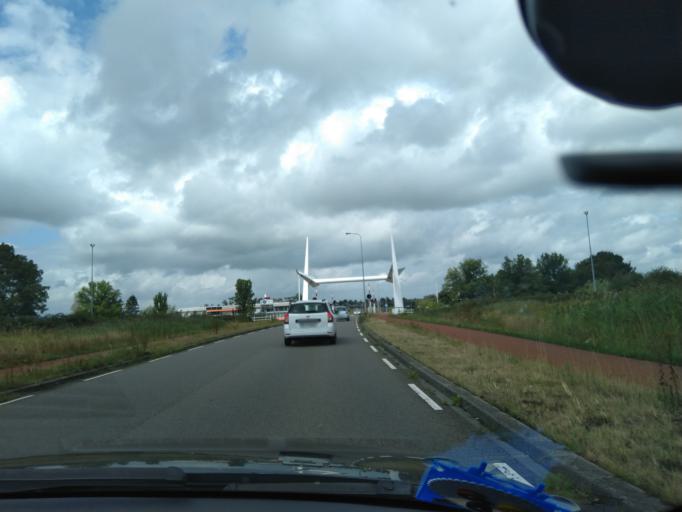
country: NL
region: Groningen
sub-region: Gemeente Groningen
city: Groningen
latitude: 53.2140
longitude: 6.5131
